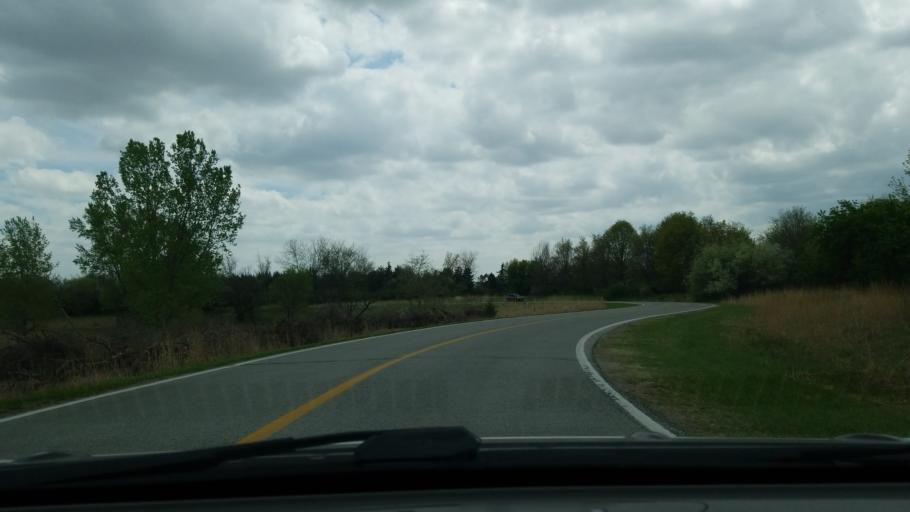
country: US
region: Nebraska
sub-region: Sarpy County
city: Chalco
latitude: 41.1672
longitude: -96.1658
